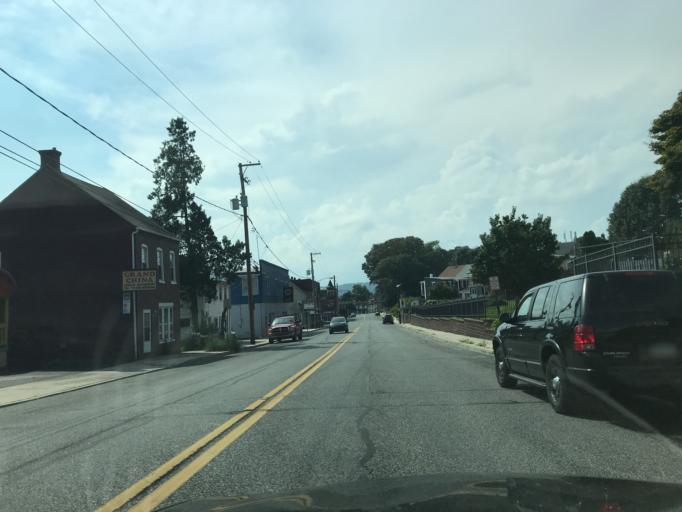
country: US
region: Pennsylvania
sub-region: Lancaster County
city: Columbia
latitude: 40.0327
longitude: -76.4959
